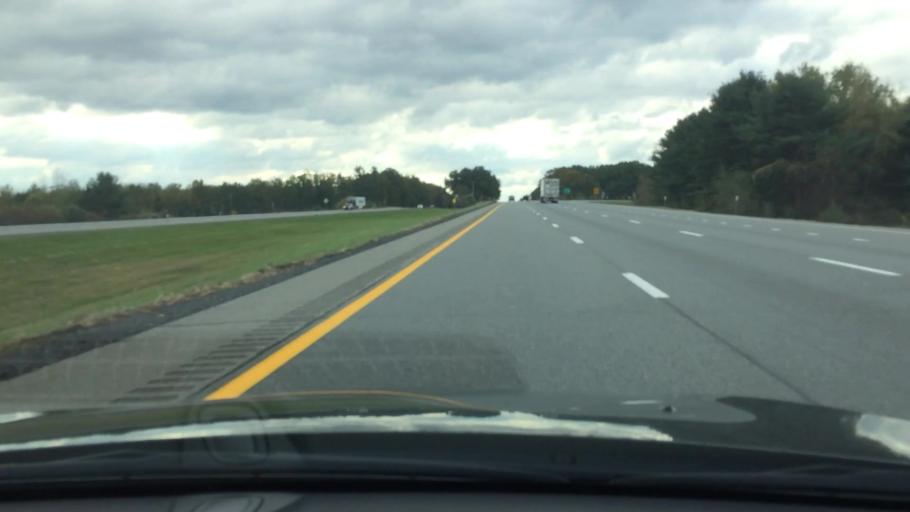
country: US
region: New York
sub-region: Saratoga County
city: Country Knolls
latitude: 42.9405
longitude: -73.8052
